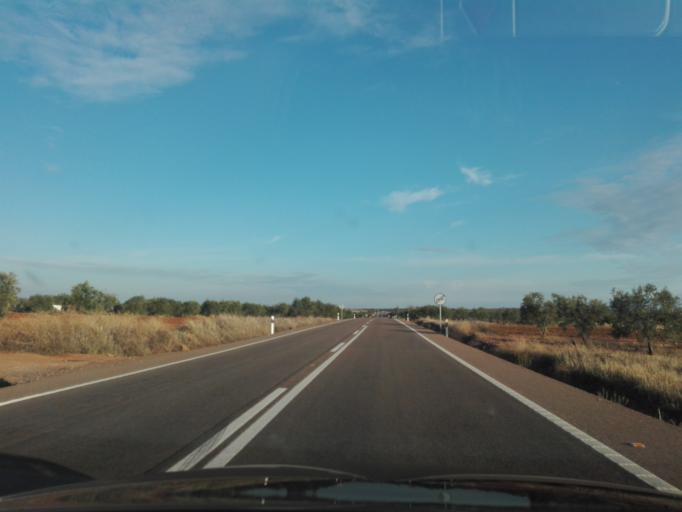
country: ES
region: Extremadura
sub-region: Provincia de Badajoz
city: Usagre
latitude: 38.3538
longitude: -6.2010
